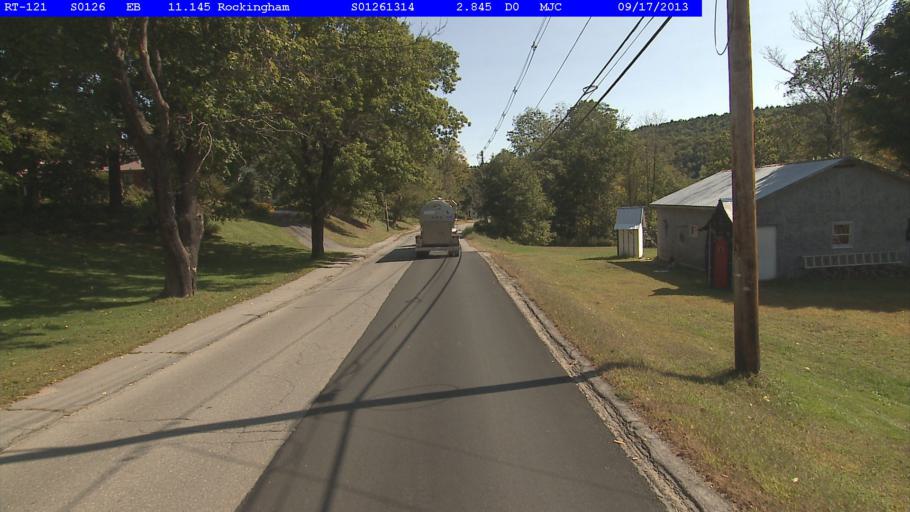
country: US
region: Vermont
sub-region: Windham County
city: Rockingham
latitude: 43.1383
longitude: -72.5122
